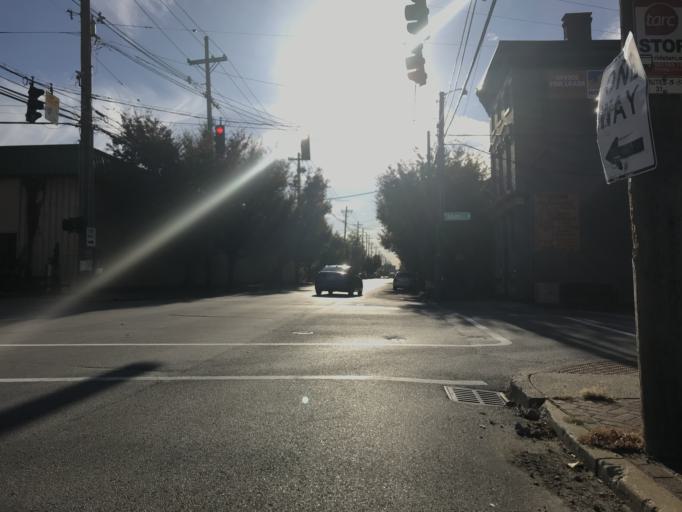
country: US
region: Indiana
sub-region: Clark County
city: Jeffersonville
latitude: 38.2574
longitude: -85.7248
